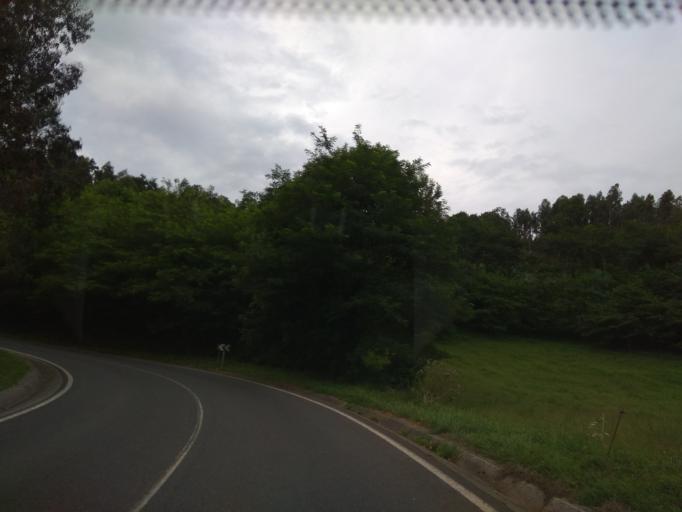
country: ES
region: Cantabria
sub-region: Provincia de Cantabria
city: Hazas de Cesto
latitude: 43.4048
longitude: -3.5973
